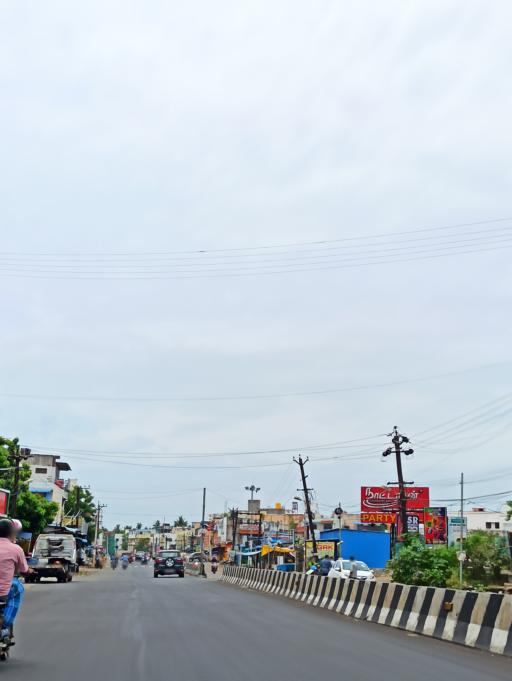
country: IN
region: Tamil Nadu
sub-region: Kancheepuram
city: Vandalur
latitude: 12.9215
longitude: 80.0920
